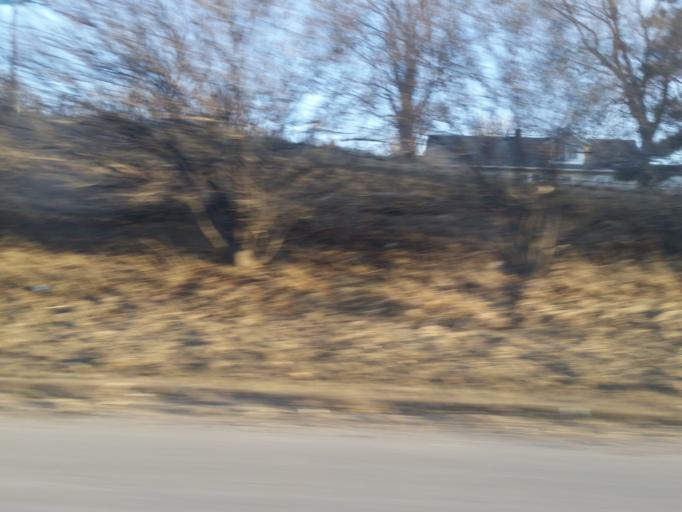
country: US
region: Nebraska
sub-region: Douglas County
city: Omaha
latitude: 41.2262
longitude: -95.9425
